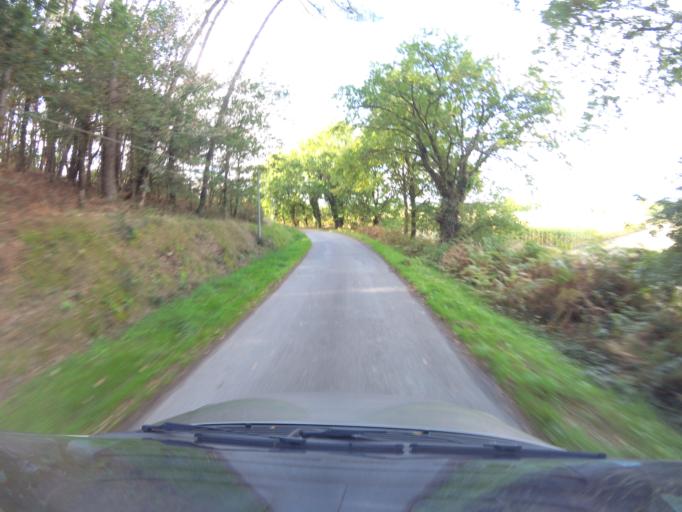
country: FR
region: Brittany
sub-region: Departement du Morbihan
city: Saint-Martin-sur-Oust
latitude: 47.7325
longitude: -2.2420
